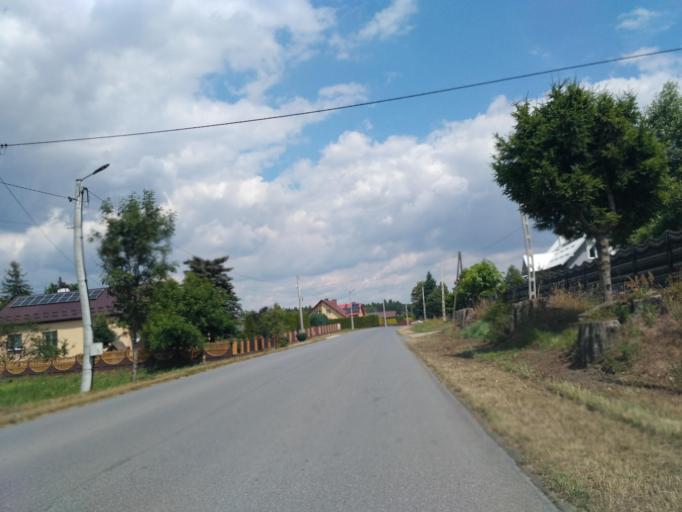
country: PL
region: Subcarpathian Voivodeship
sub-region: Powiat debicki
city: Pilzno
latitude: 50.0138
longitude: 21.2892
